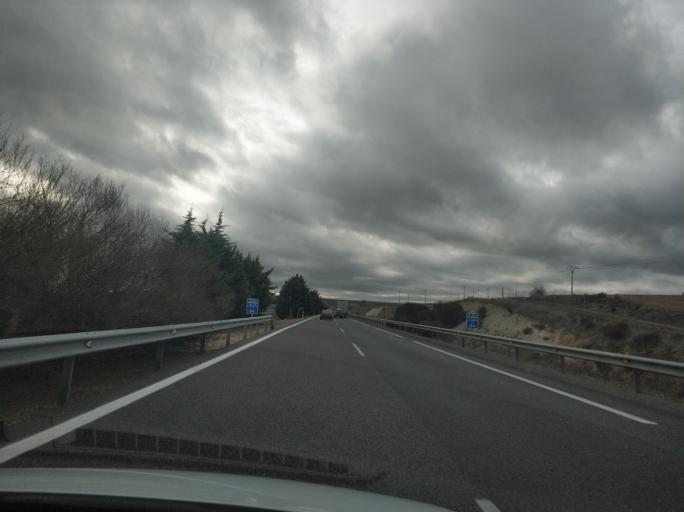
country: ES
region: Castille and Leon
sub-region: Provincia de Palencia
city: Venta de Banos
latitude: 41.9458
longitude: -4.4756
